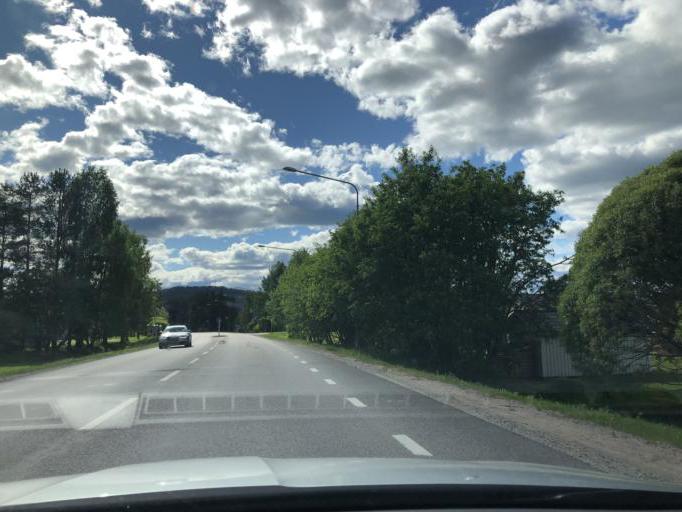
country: SE
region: Norrbotten
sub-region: Alvsbyns Kommun
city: AElvsbyn
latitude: 65.6712
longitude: 21.0032
